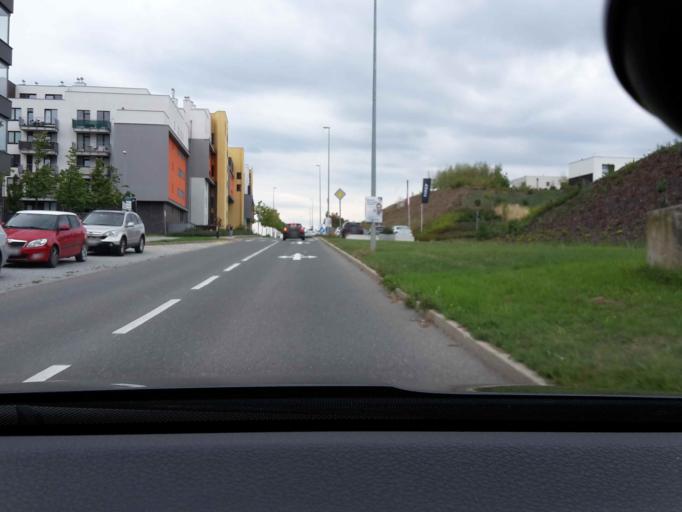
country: CZ
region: Central Bohemia
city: Hostivice
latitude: 50.0486
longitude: 14.3050
